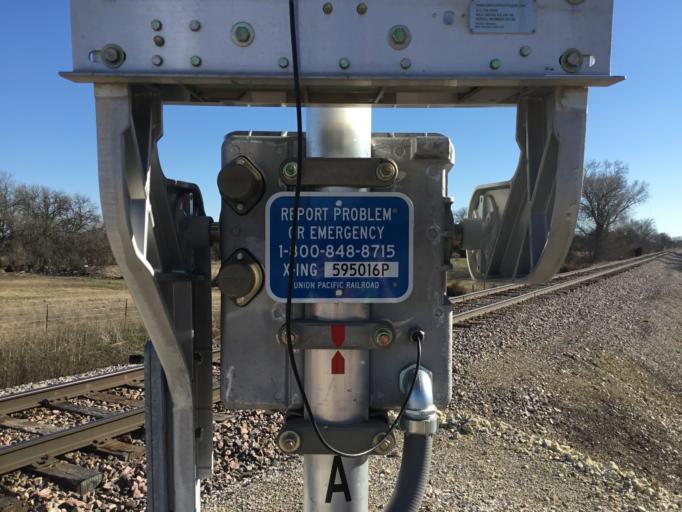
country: US
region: Kansas
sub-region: Sedgwick County
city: Kechi
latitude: 37.8250
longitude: -97.2547
